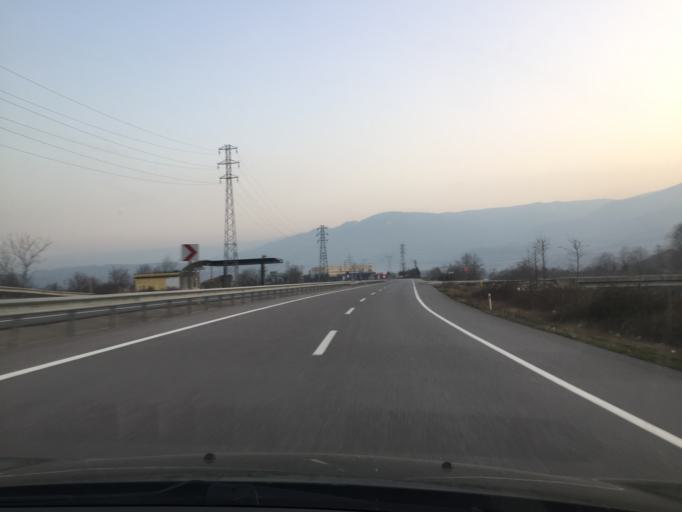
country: TR
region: Sakarya
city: Akyazi
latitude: 40.6447
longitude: 30.6124
